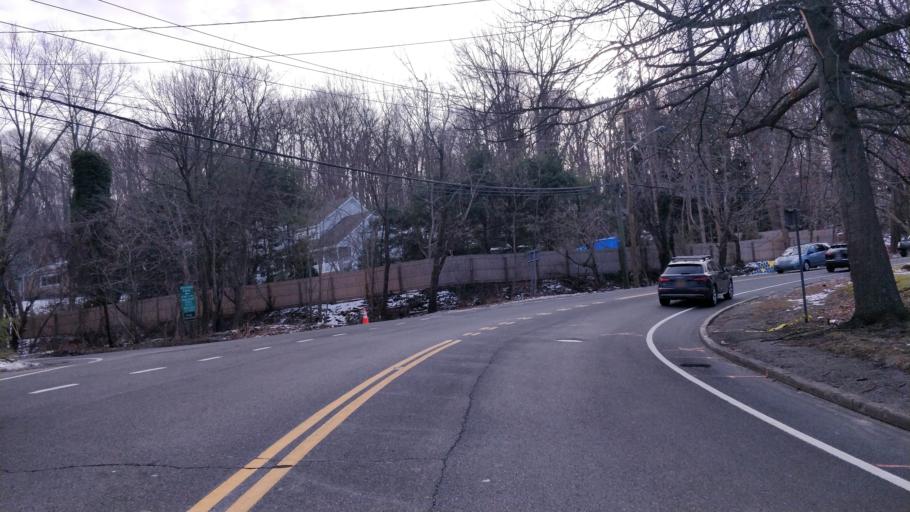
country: US
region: New York
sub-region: Suffolk County
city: Northport
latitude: 40.8890
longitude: -73.3551
